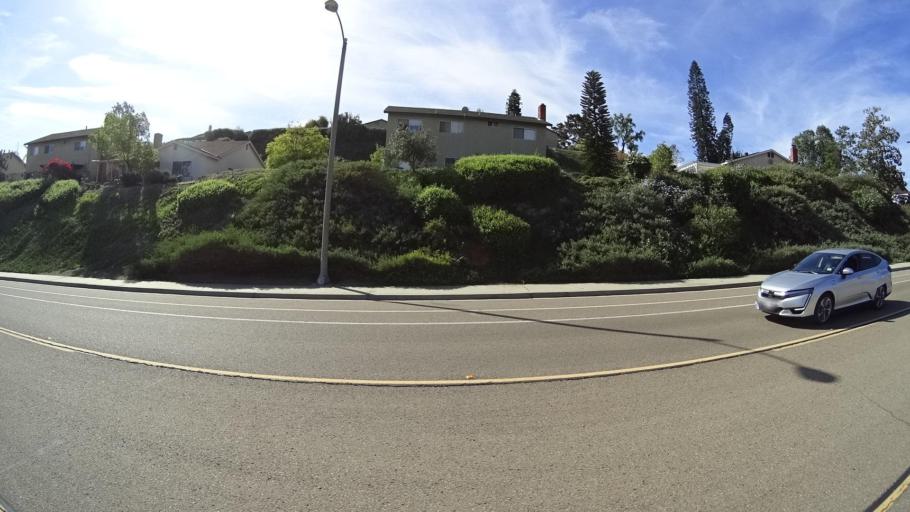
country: US
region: California
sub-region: San Diego County
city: Spring Valley
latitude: 32.7311
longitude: -116.9811
